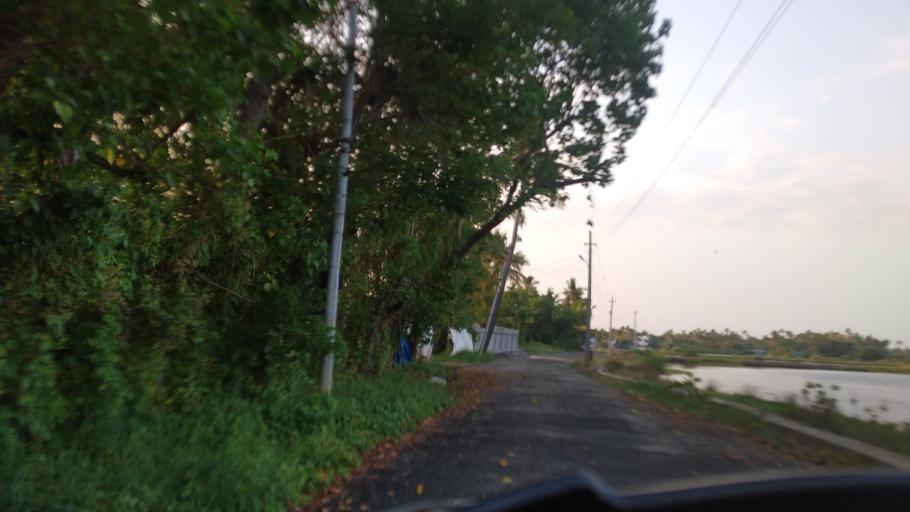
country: IN
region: Kerala
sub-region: Ernakulam
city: Elur
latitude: 10.0500
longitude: 76.2270
